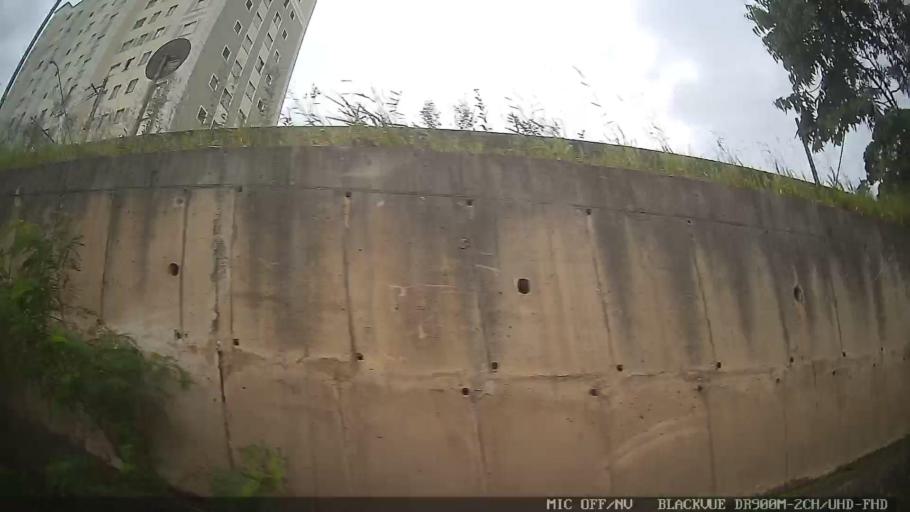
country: BR
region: Sao Paulo
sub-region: Maua
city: Maua
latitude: -23.6745
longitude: -46.4699
